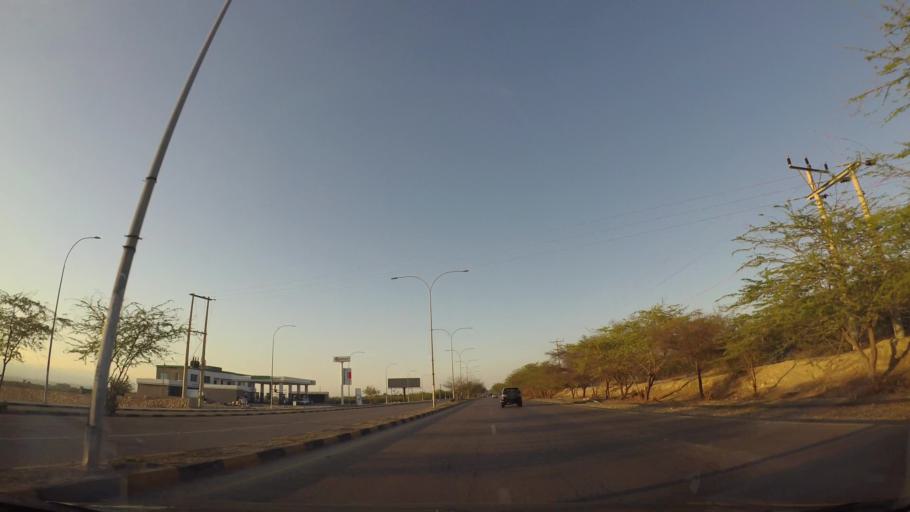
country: PS
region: West Bank
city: Jericho
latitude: 31.7784
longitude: 35.5923
